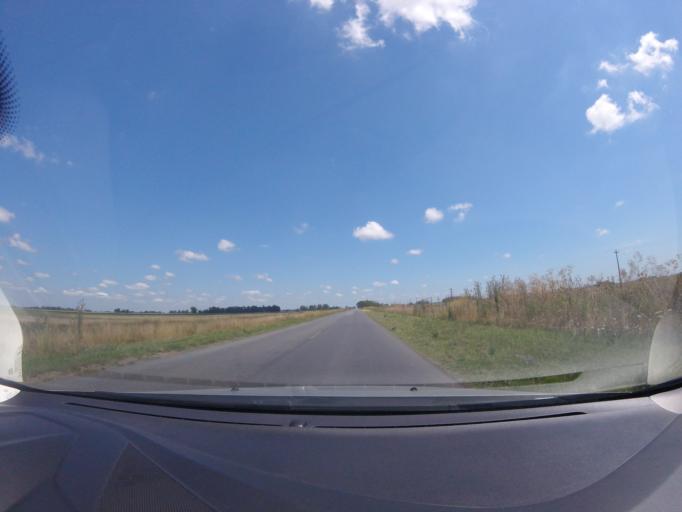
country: AR
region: Buenos Aires
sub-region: Partido de Rauch
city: Rauch
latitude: -36.8379
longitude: -58.9972
